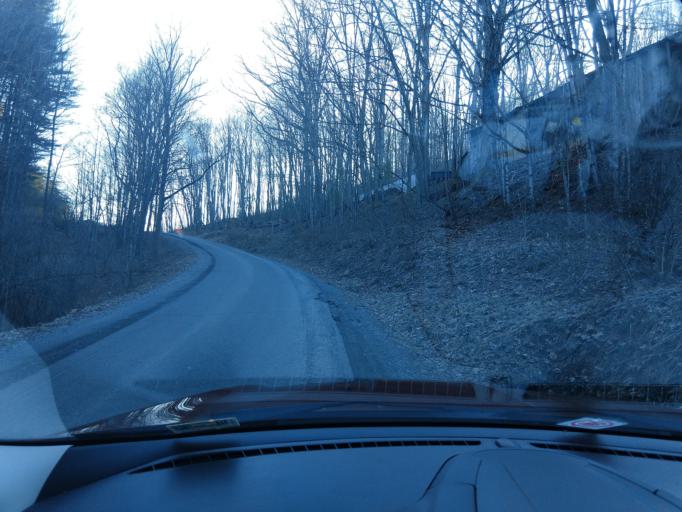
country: US
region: West Virginia
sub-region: Greenbrier County
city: Rainelle
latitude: 37.9222
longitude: -80.7414
